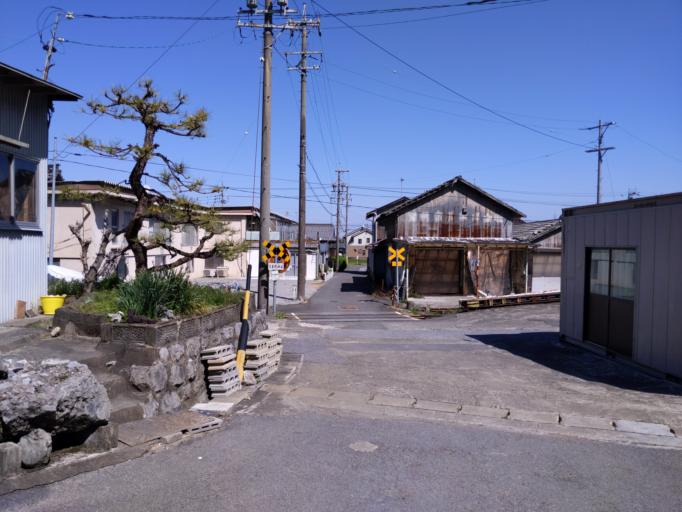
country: JP
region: Gifu
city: Godo
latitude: 35.3945
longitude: 136.5806
